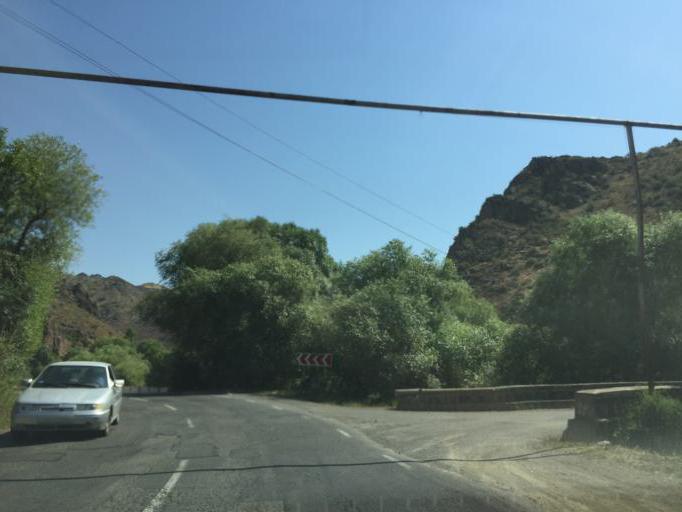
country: AM
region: Vayots' Dzori Marz
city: Vayk'
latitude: 39.6821
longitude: 45.4877
